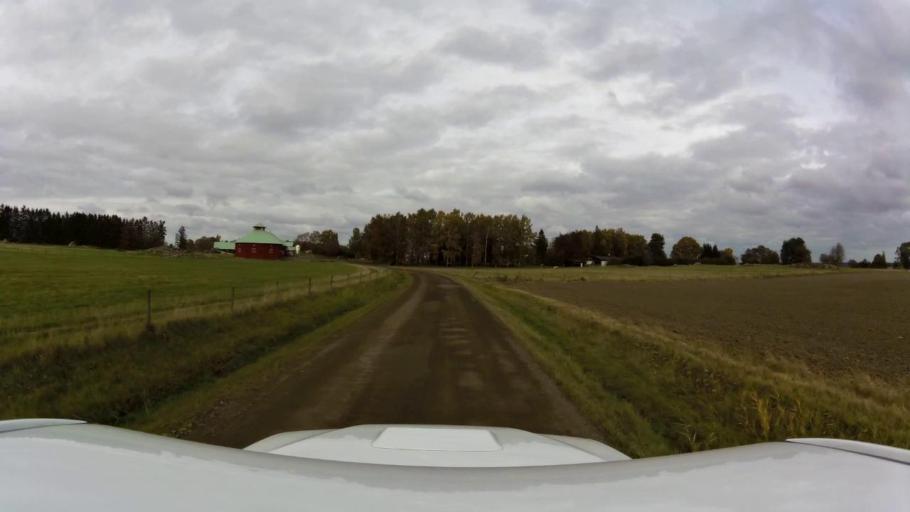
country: SE
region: OEstergoetland
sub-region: Linkopings Kommun
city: Linkoping
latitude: 58.4462
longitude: 15.5877
